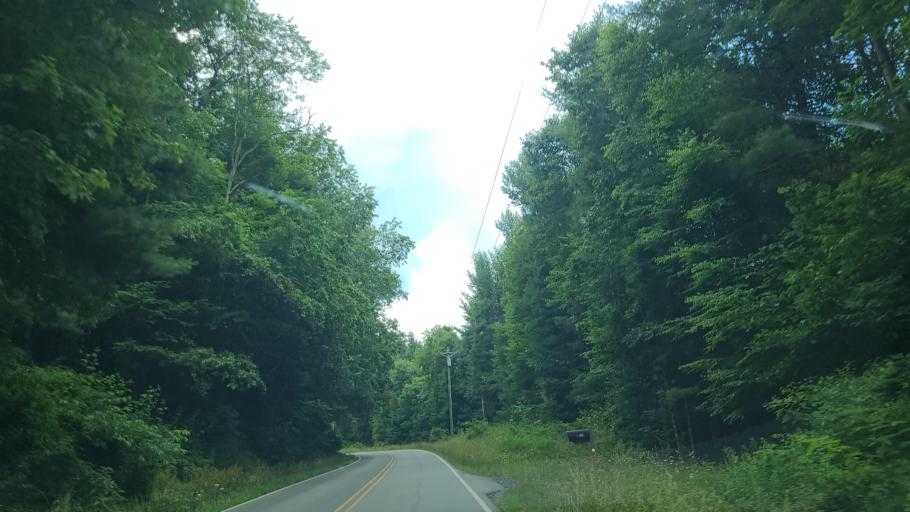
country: US
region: North Carolina
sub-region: Ashe County
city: Jefferson
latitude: 36.3919
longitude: -81.3469
